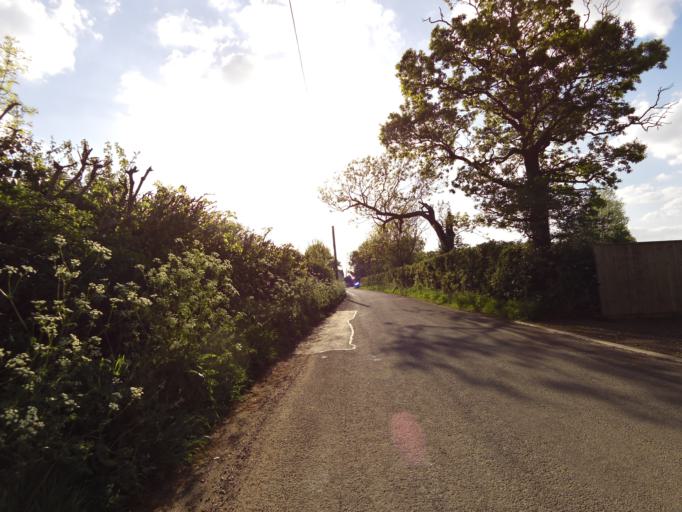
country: GB
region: England
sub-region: Suffolk
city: Beccles
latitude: 52.4217
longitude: 1.5085
